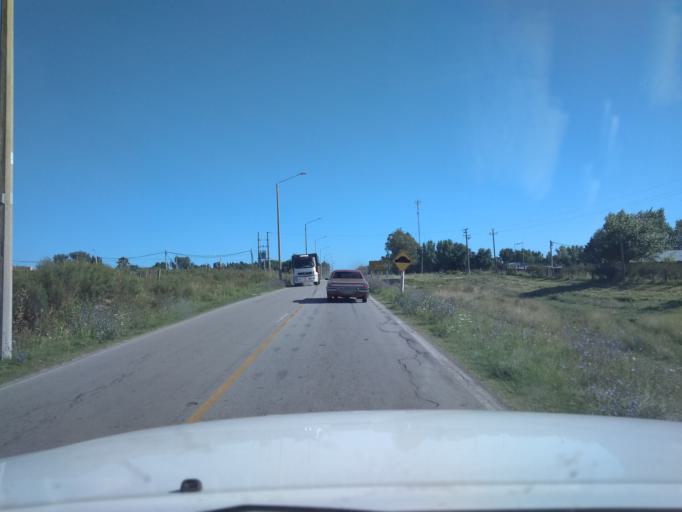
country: UY
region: Canelones
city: San Ramon
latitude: -34.3108
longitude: -55.9587
